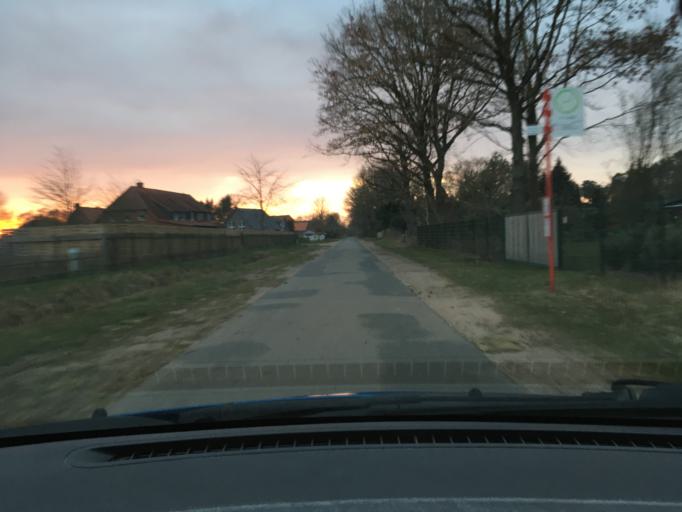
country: DE
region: Lower Saxony
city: Bleckede
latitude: 53.2927
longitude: 10.6897
